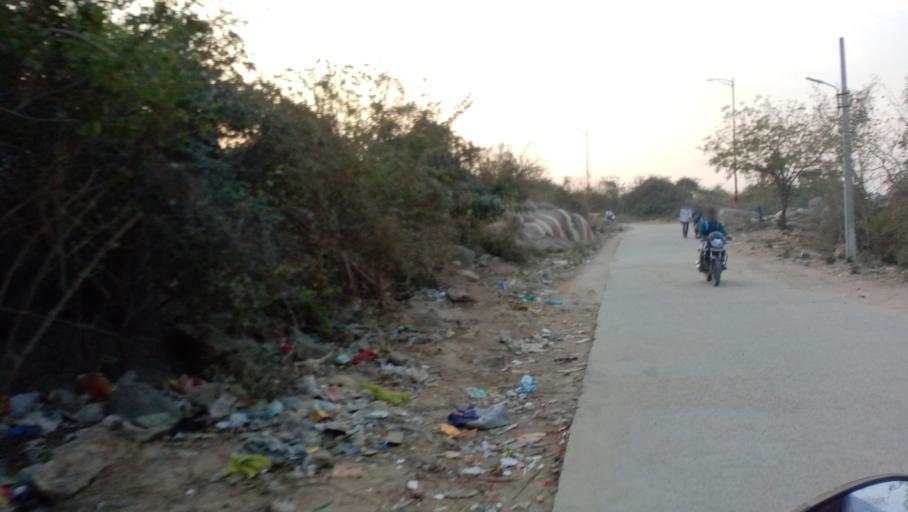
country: IN
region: Telangana
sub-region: Medak
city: Serilingampalle
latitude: 17.5204
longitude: 78.3079
